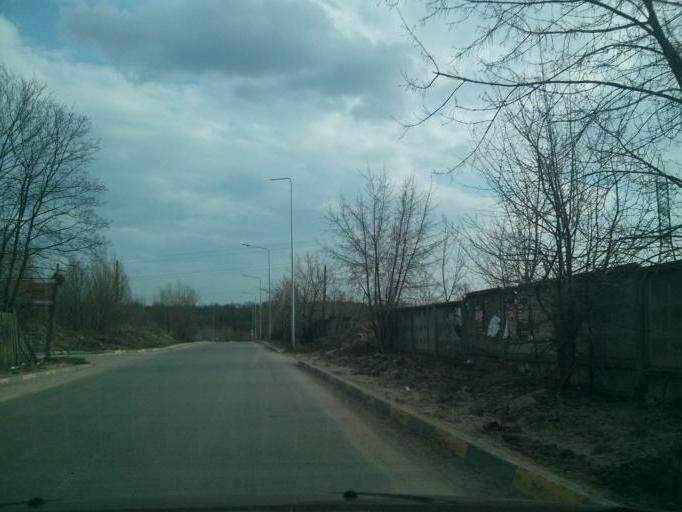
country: RU
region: Nizjnij Novgorod
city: Nizhniy Novgorod
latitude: 56.2599
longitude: 44.0093
